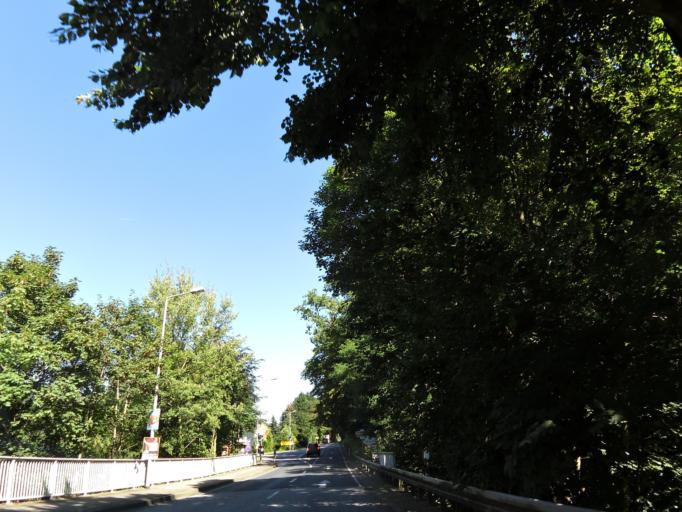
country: DE
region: Saxony
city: Kurort Gohrisch
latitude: 50.9248
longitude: 14.0955
